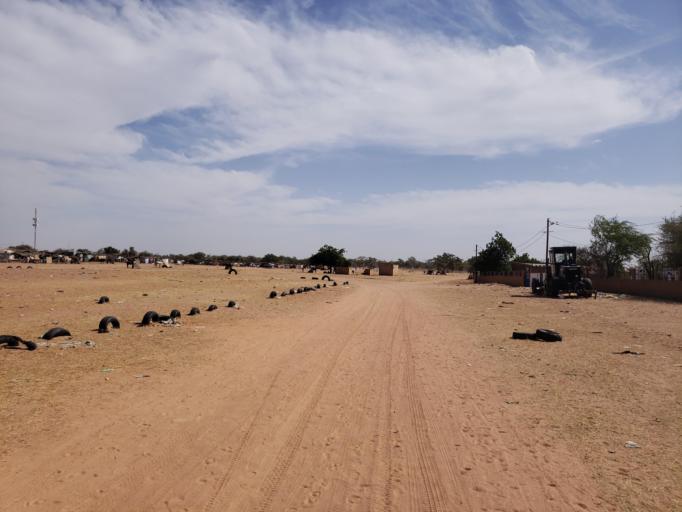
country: SN
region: Matam
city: Ranerou
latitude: 15.2969
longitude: -13.9631
